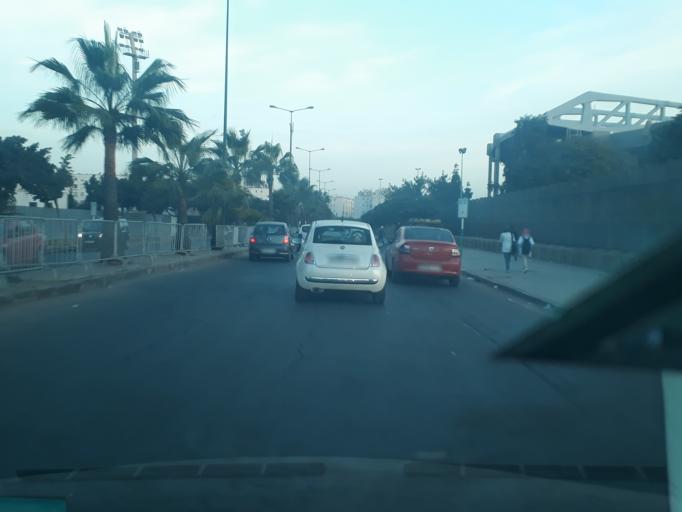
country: MA
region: Grand Casablanca
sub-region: Casablanca
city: Casablanca
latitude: 33.5810
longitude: -7.6476
